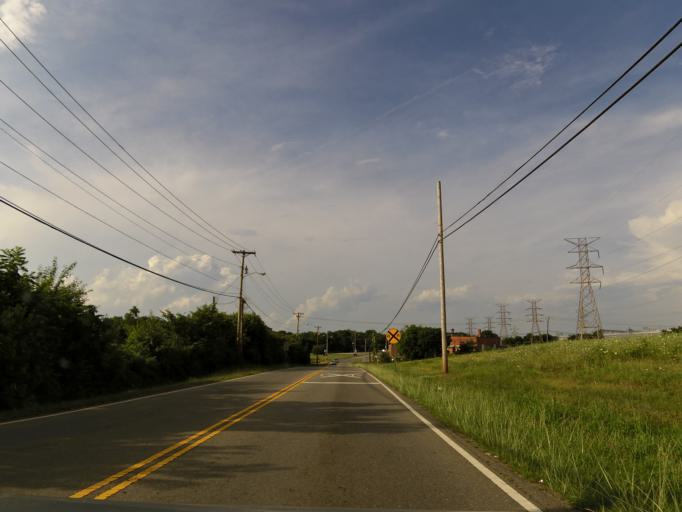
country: US
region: Tennessee
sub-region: Blount County
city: Maryville
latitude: 35.7698
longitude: -83.9802
